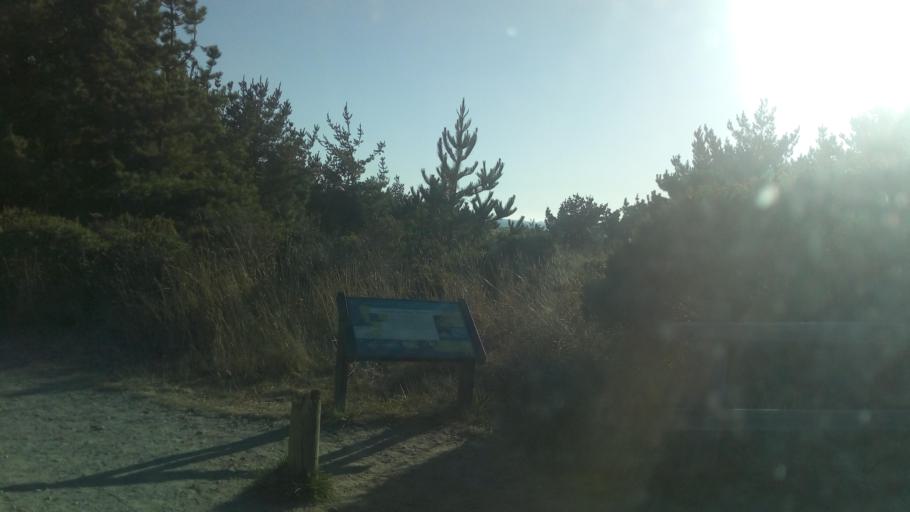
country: US
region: California
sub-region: Marin County
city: Inverness
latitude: 38.0289
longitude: -122.8827
